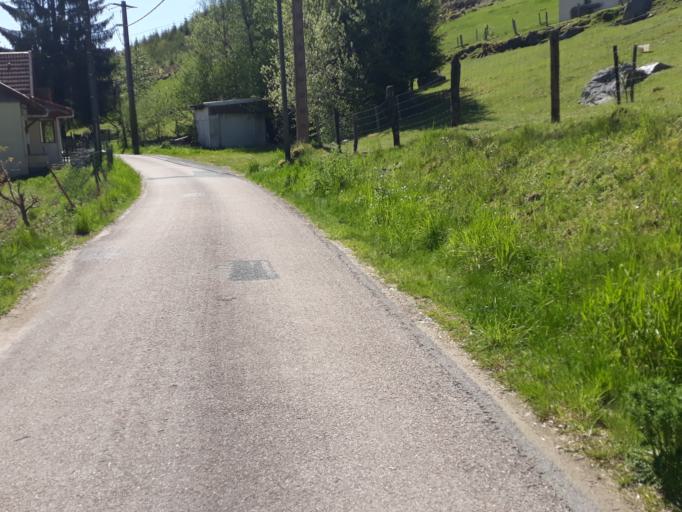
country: FR
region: Lorraine
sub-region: Departement des Vosges
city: Granges-sur-Vologne
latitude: 48.1414
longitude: 6.7839
